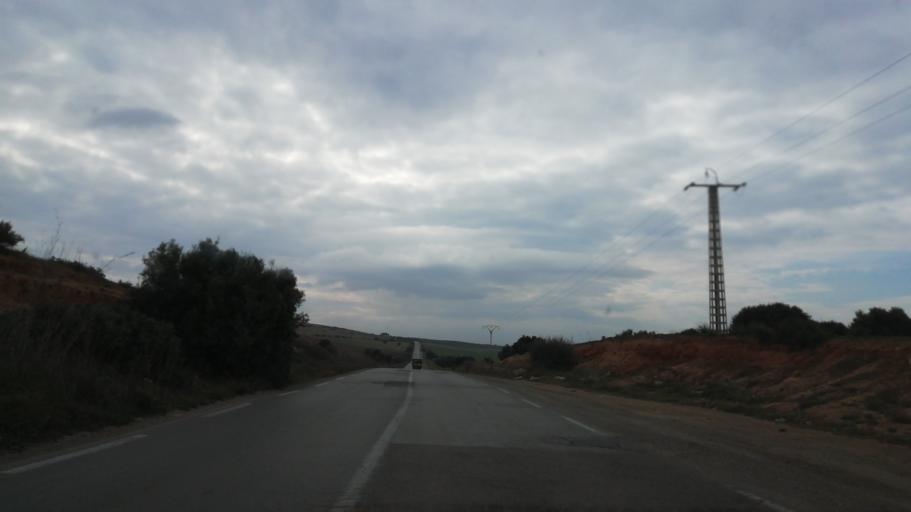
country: DZ
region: Oran
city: Ain el Bya
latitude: 35.7463
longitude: -0.3543
